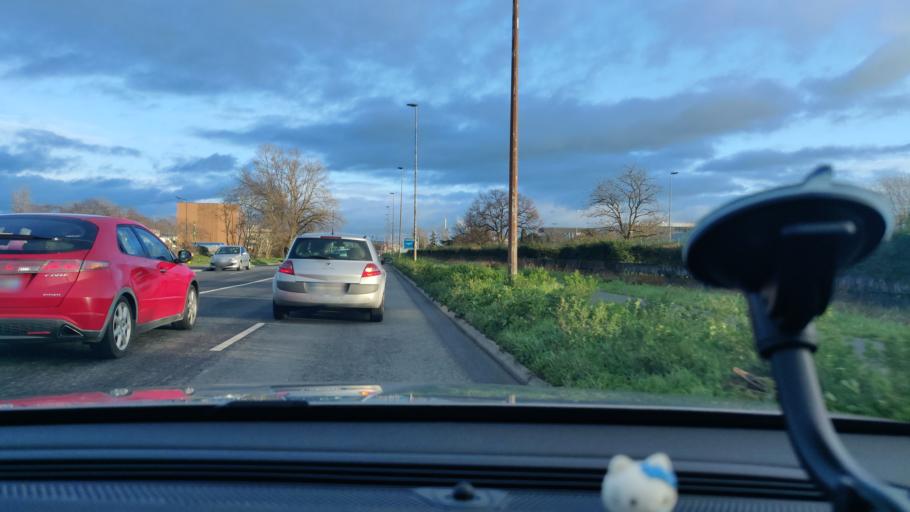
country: FR
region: Midi-Pyrenees
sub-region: Departement de la Haute-Garonne
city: Cugnaux
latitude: 43.5661
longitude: 1.3803
